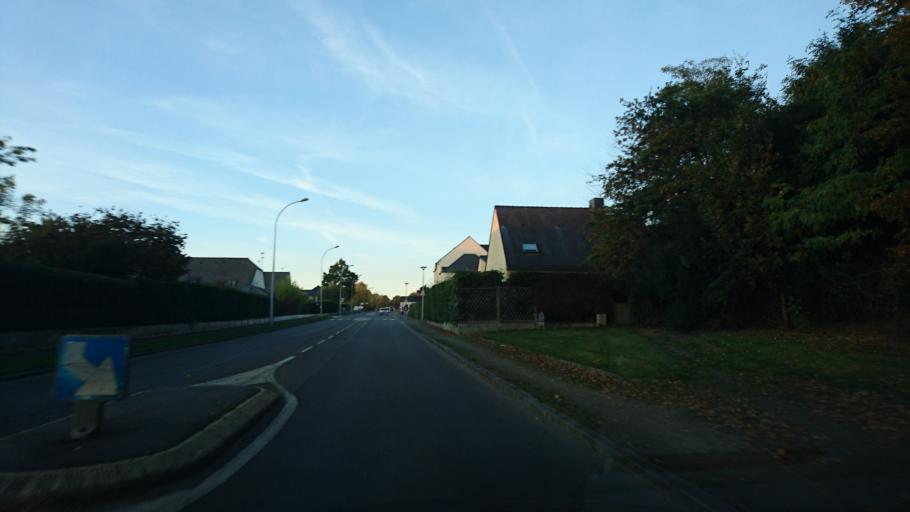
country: FR
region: Brittany
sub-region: Departement d'Ille-et-Vilaine
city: Bruz
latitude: 48.0224
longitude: -1.7526
